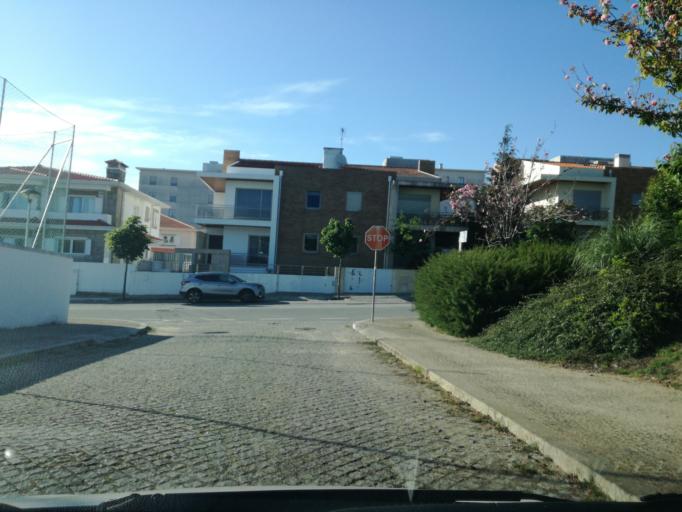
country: PT
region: Porto
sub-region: Maia
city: Gemunde
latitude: 41.2592
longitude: -8.6653
